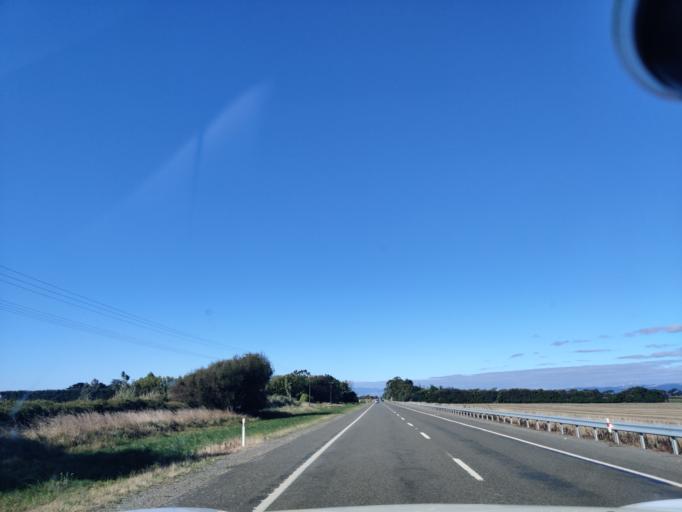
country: NZ
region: Manawatu-Wanganui
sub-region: Palmerston North City
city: Palmerston North
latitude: -40.3976
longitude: 175.5118
